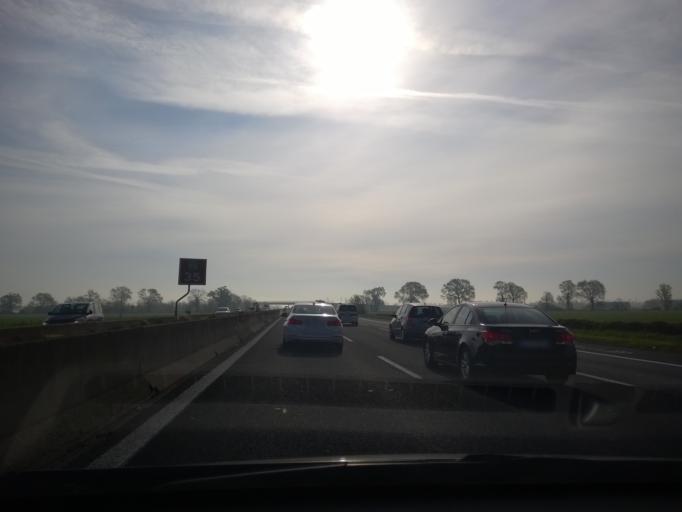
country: IT
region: Emilia-Romagna
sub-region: Provincia di Bologna
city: Toscanella
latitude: 44.4141
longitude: 11.6363
